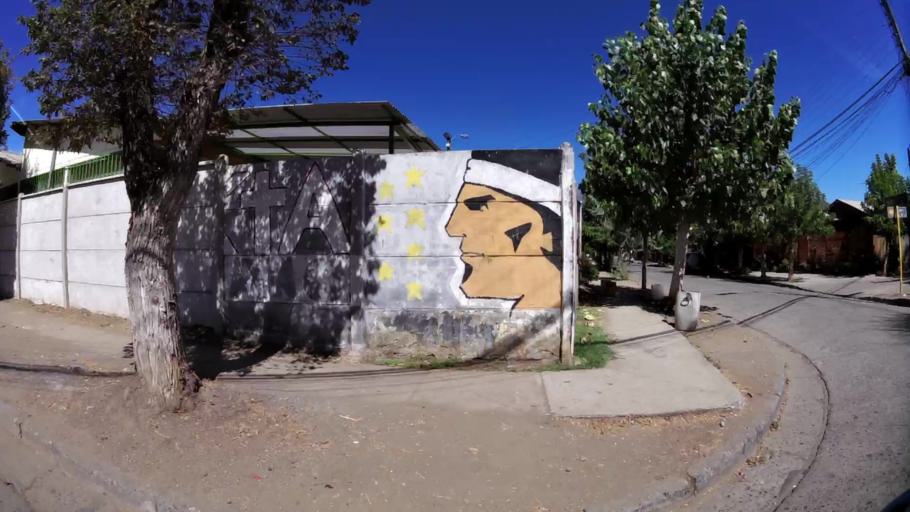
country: CL
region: O'Higgins
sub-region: Provincia de Cachapoal
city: Graneros
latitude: -33.9713
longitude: -70.7106
